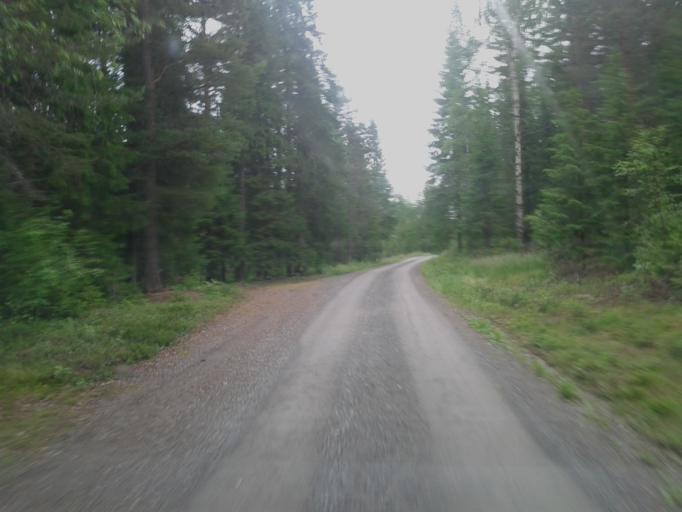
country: SE
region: Vaesternorrland
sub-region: OErnskoeldsviks Kommun
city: Bjasta
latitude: 63.0756
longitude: 18.4529
